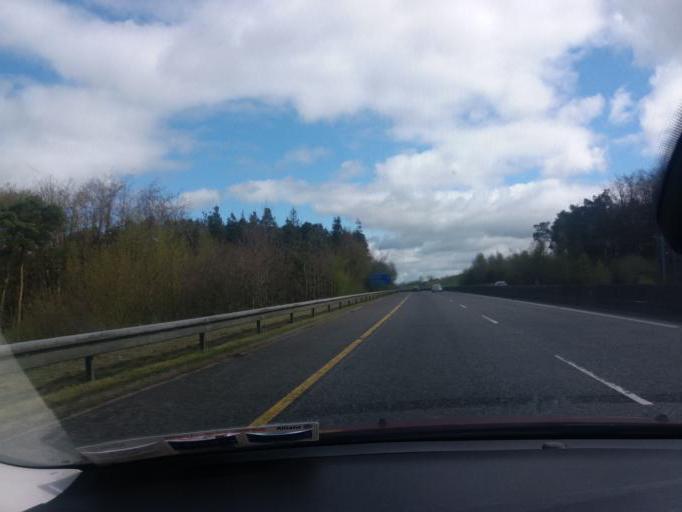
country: IE
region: Munster
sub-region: County Cork
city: Fermoy
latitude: 52.1227
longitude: -8.2665
